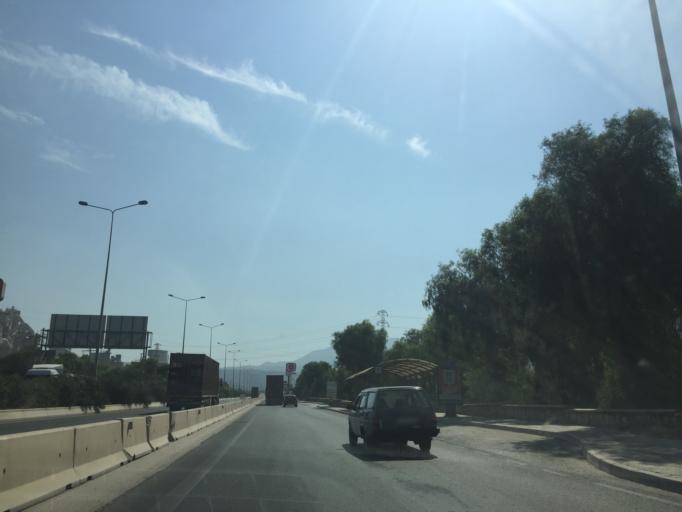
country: TR
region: Izmir
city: Bornova
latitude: 38.4558
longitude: 27.2563
